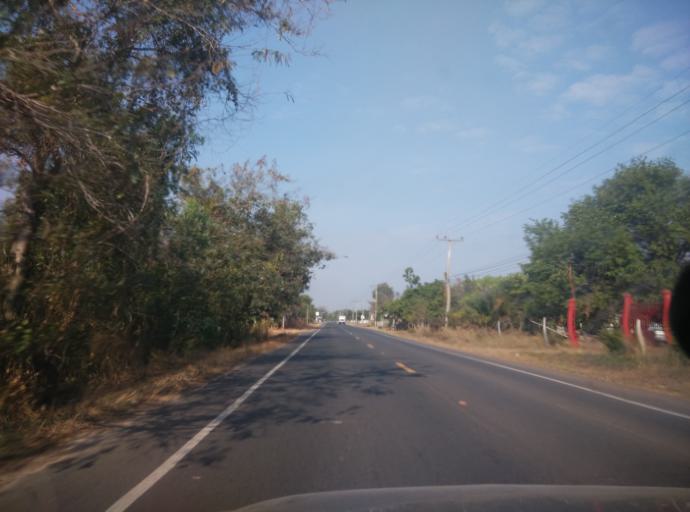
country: TH
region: Sisaket
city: Si Sa Ket
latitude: 15.1148
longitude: 104.2643
